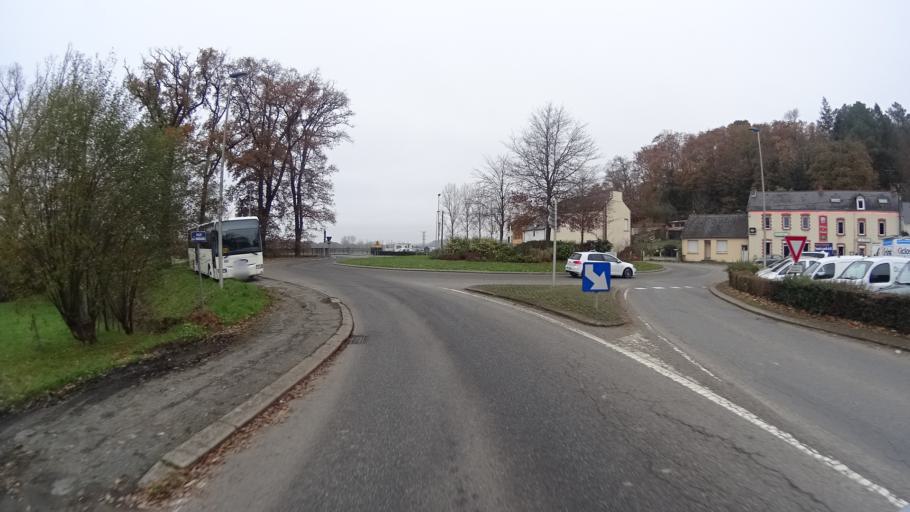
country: FR
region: Brittany
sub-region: Departement du Morbihan
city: Saint-Perreux
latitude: 47.6620
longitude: -2.0984
